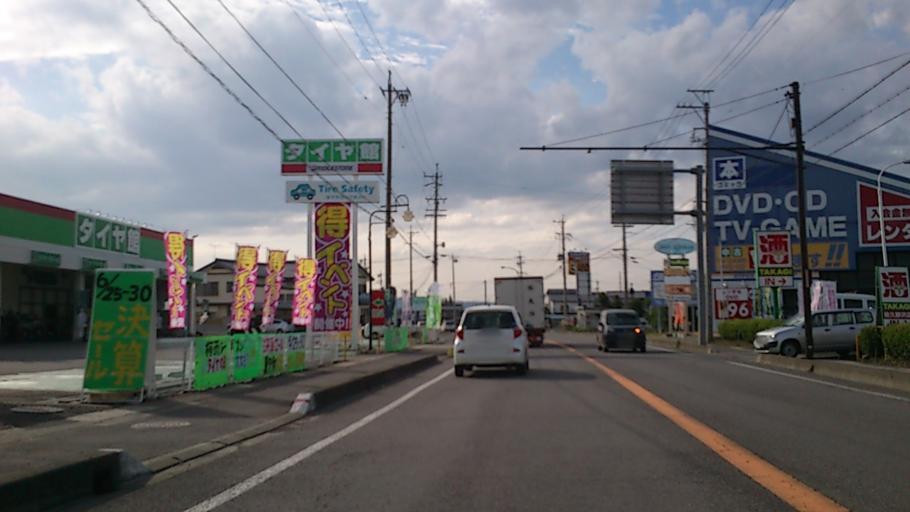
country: JP
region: Nagano
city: Saku
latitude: 36.2282
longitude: 138.4653
